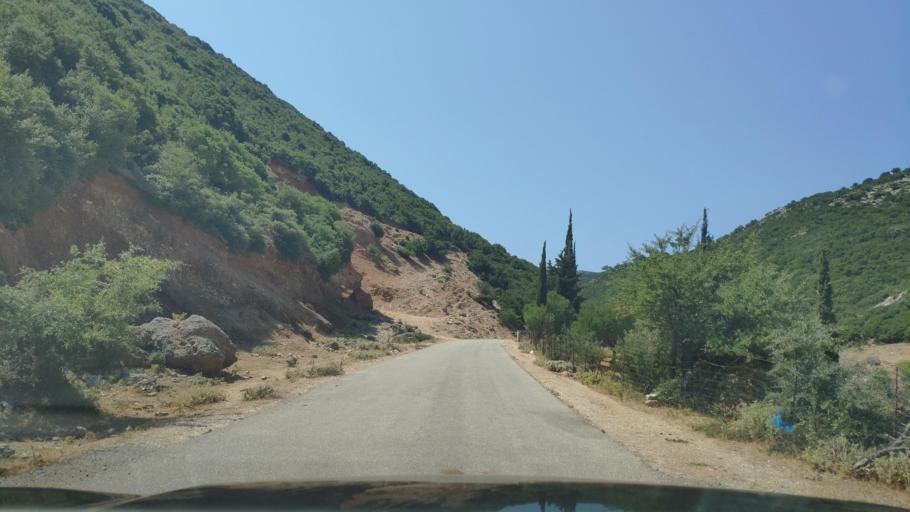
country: GR
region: West Greece
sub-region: Nomos Aitolias kai Akarnanias
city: Monastirakion
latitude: 38.8396
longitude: 20.9358
